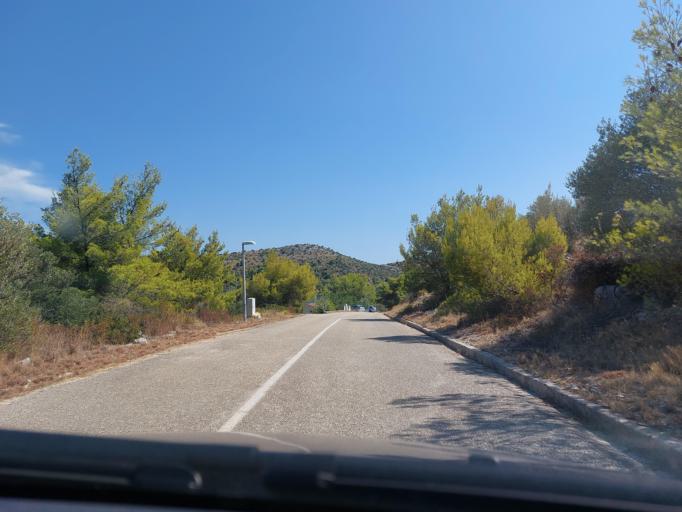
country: HR
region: Dubrovacko-Neretvanska
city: Smokvica
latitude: 42.7360
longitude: 16.8849
